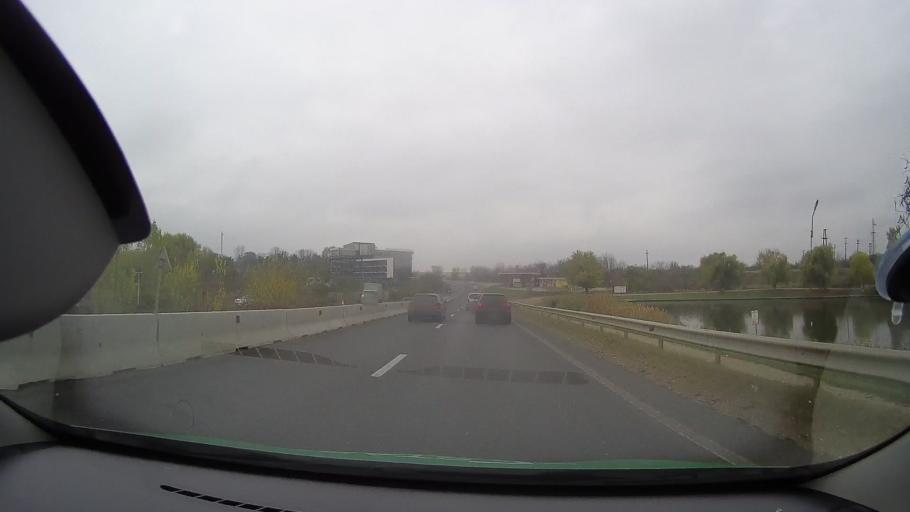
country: RO
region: Ilfov
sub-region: Comuna Ciolpani
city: Ciolpani
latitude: 44.6743
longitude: 26.0744
